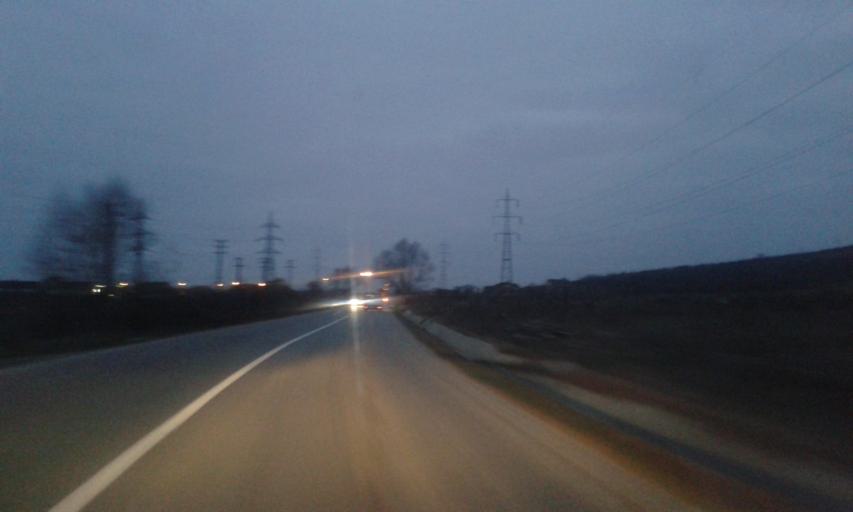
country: RO
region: Gorj
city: Targu Jiu
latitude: 45.0549
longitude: 23.2644
